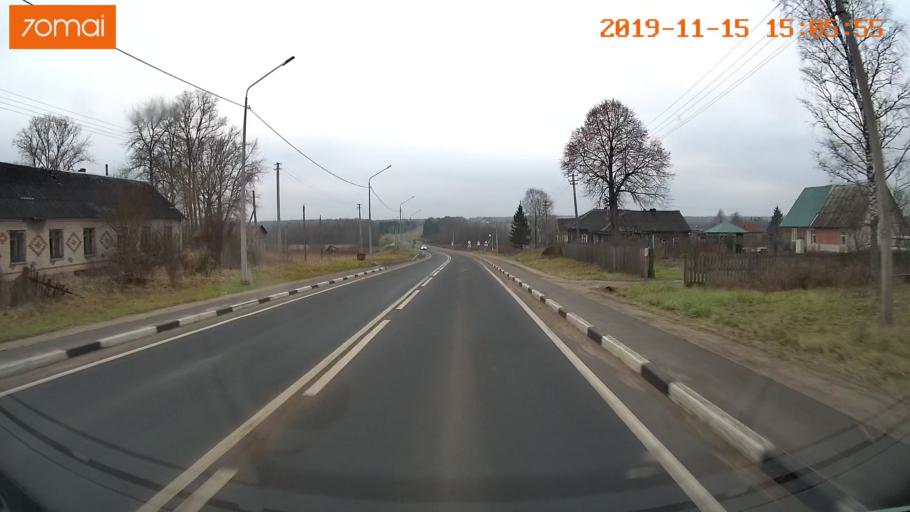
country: RU
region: Jaroslavl
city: Prechistoye
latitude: 58.3984
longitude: 40.3177
